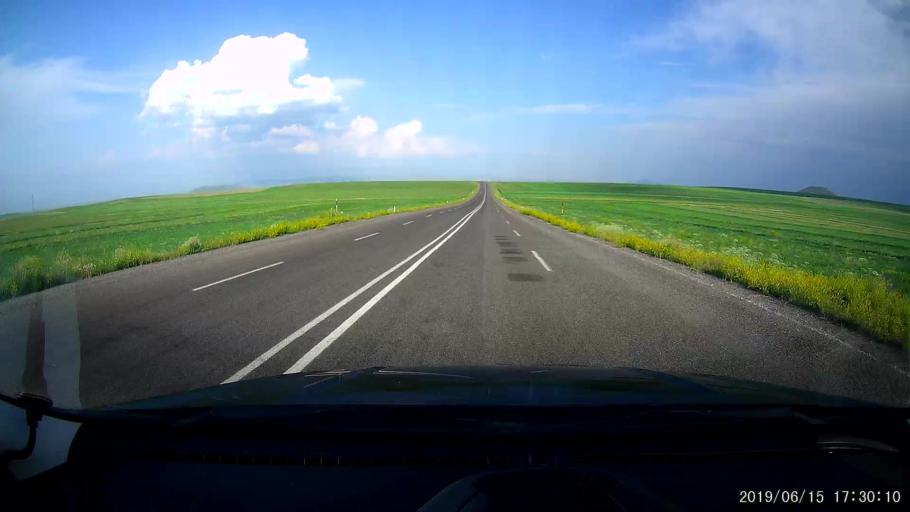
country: TR
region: Kars
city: Basgedikler
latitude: 40.5843
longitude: 43.4642
